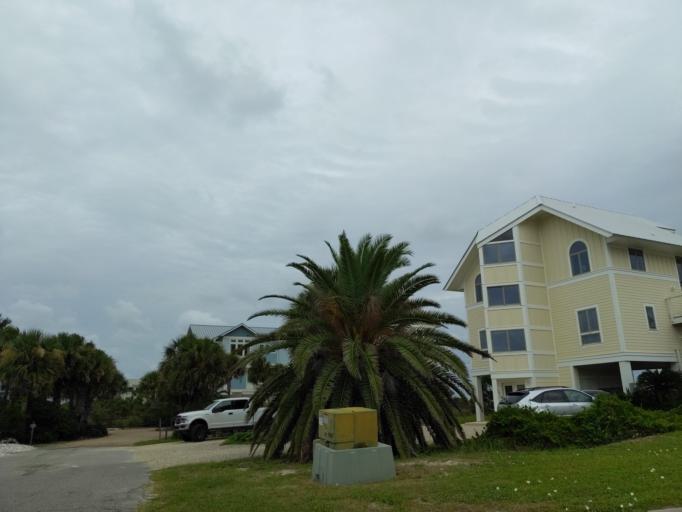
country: US
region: Florida
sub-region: Franklin County
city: Apalachicola
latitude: 29.6296
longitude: -84.9280
